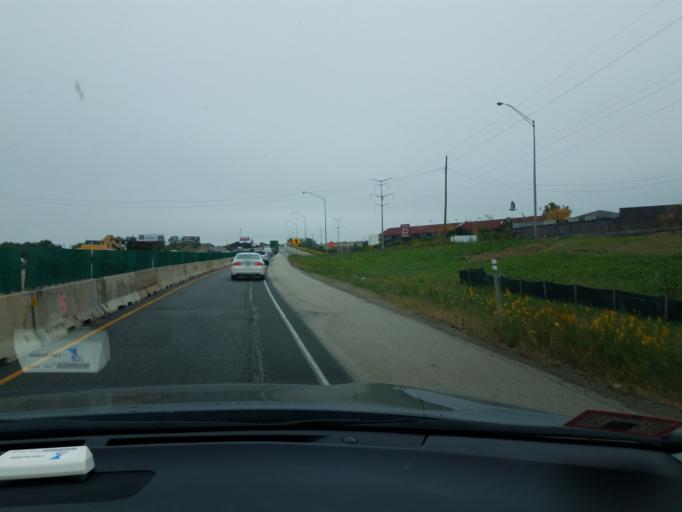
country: US
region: Illinois
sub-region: Cook County
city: Northbrook
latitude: 42.1453
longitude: -87.8314
